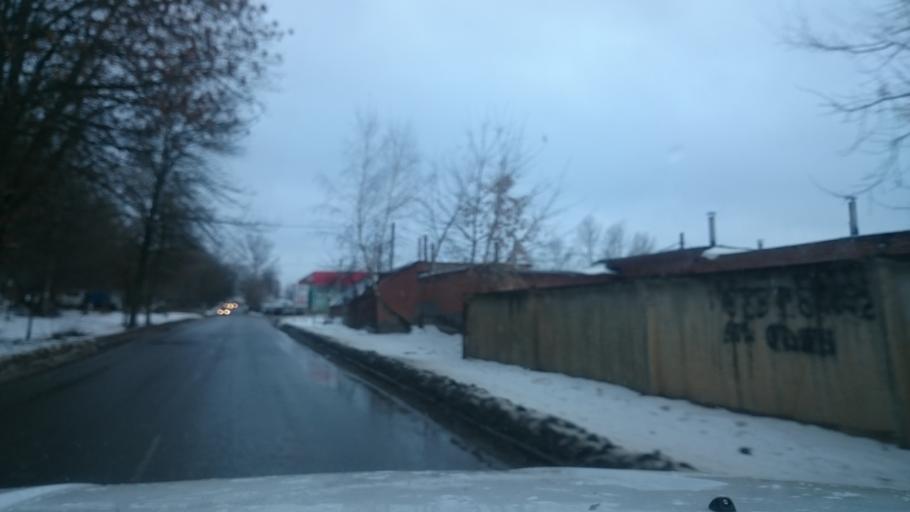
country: RU
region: Tula
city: Mendeleyevskiy
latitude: 54.1749
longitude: 37.5657
